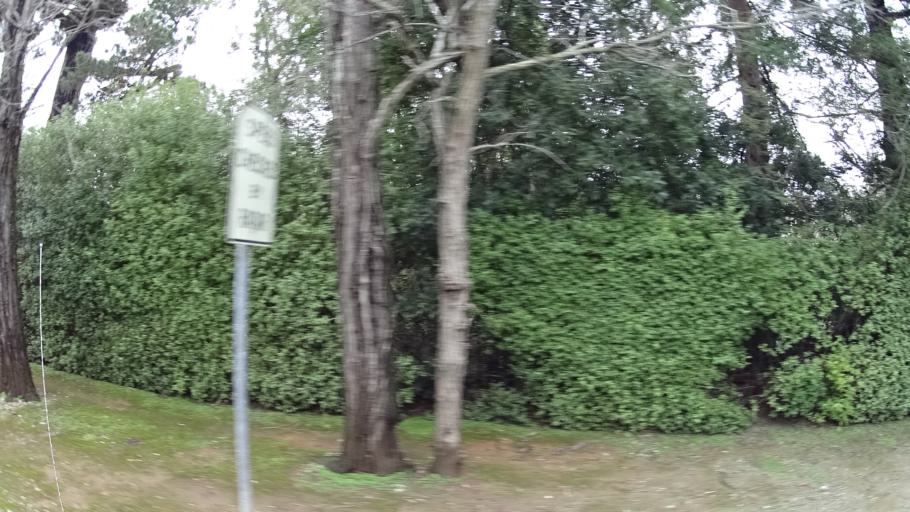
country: US
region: California
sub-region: San Mateo County
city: San Mateo
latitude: 37.5629
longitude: -122.3435
